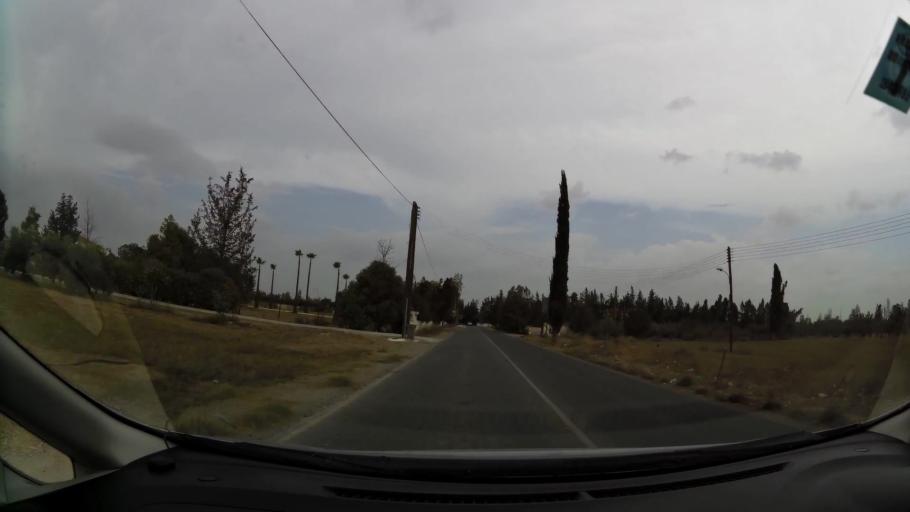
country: CY
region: Lefkosia
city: Geri
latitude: 35.0843
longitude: 33.3954
